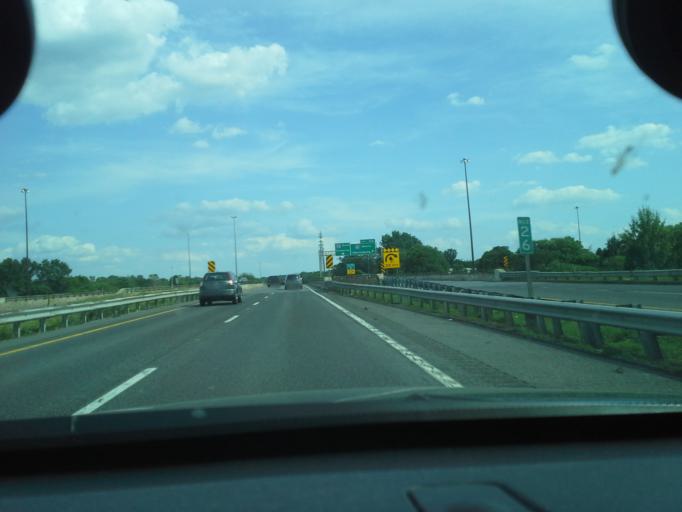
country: US
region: Maryland
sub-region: Washington County
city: Halfway
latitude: 39.6177
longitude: -77.7862
